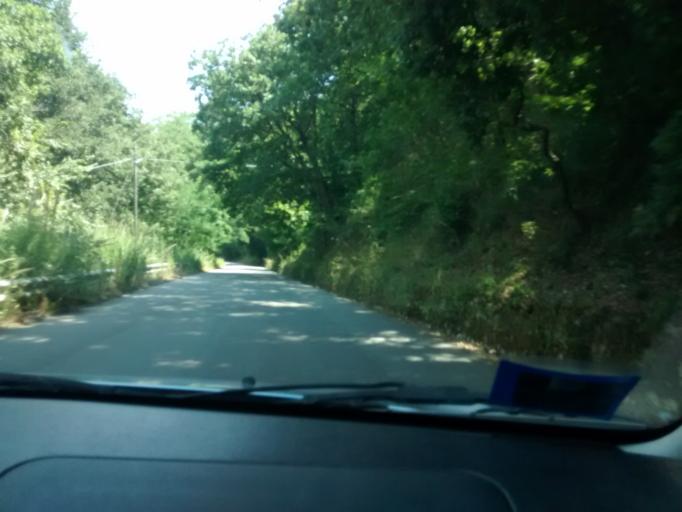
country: IT
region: Calabria
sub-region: Provincia di Catanzaro
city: Maida
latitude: 38.8995
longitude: 16.3871
